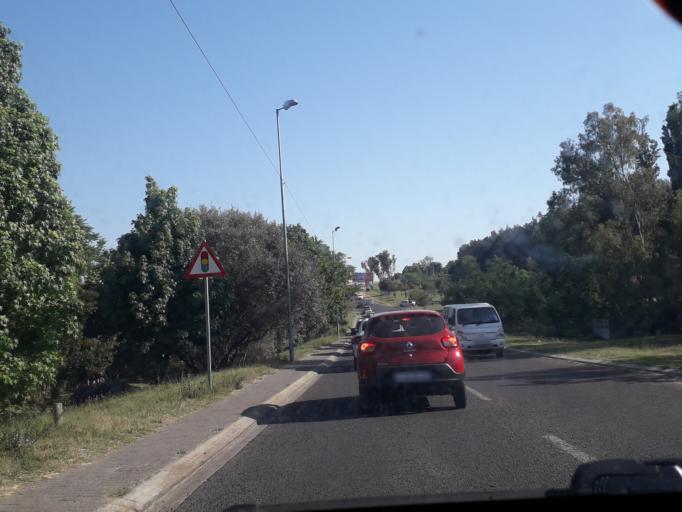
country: ZA
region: Gauteng
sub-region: City of Johannesburg Metropolitan Municipality
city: Midrand
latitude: -26.0440
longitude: 28.0697
